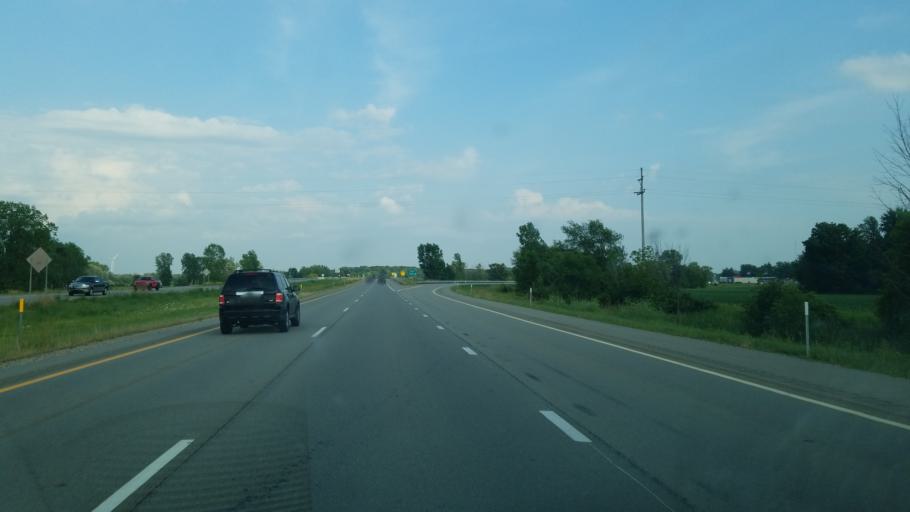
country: US
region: Michigan
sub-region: Gratiot County
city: Saint Louis
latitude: 43.3845
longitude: -84.6119
